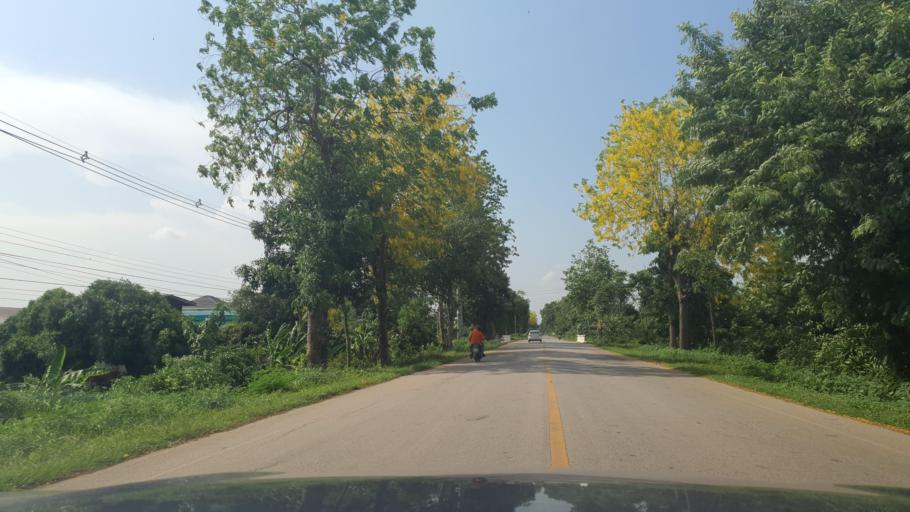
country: TH
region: Sukhothai
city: Si Samrong
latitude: 17.1811
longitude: 99.8518
